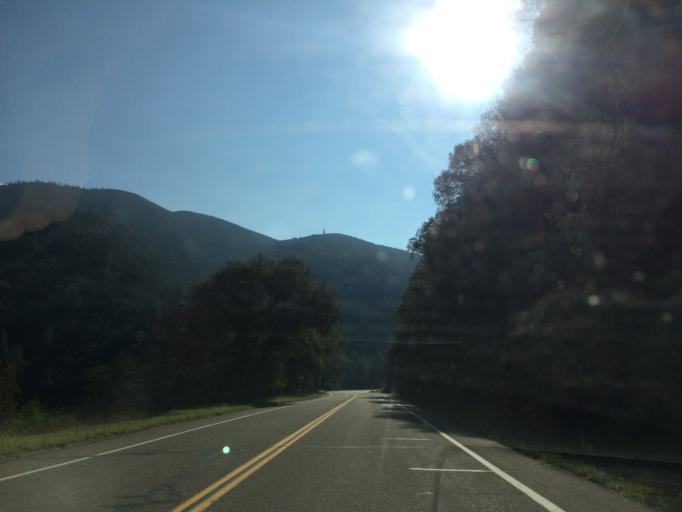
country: US
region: California
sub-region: Mariposa County
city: Midpines
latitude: 37.6004
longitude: -119.9606
